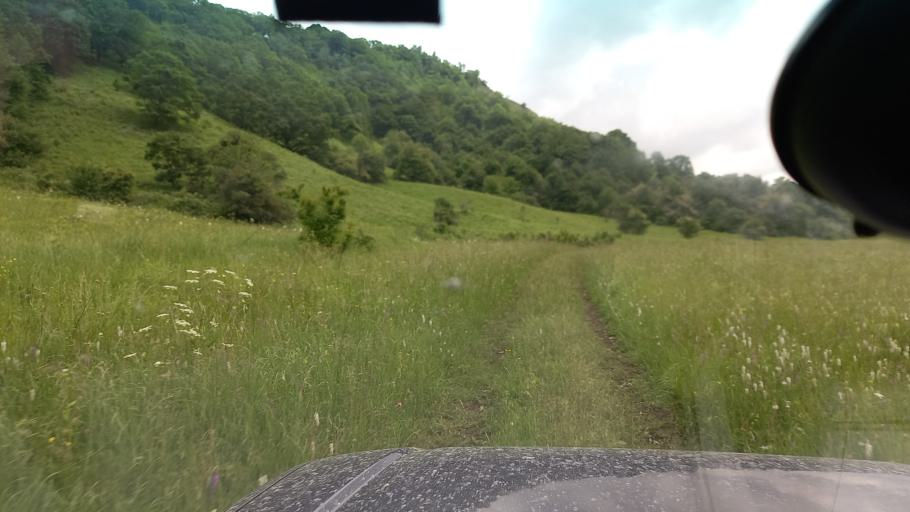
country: RU
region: Krasnodarskiy
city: Psebay
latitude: 44.1526
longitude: 40.8569
